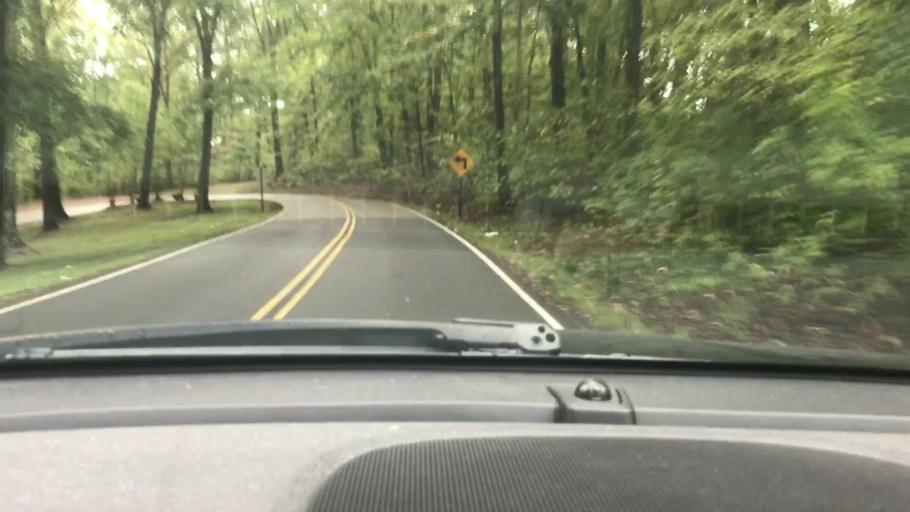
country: US
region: Tennessee
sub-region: Cheatham County
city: Kingston Springs
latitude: 36.1022
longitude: -87.1362
